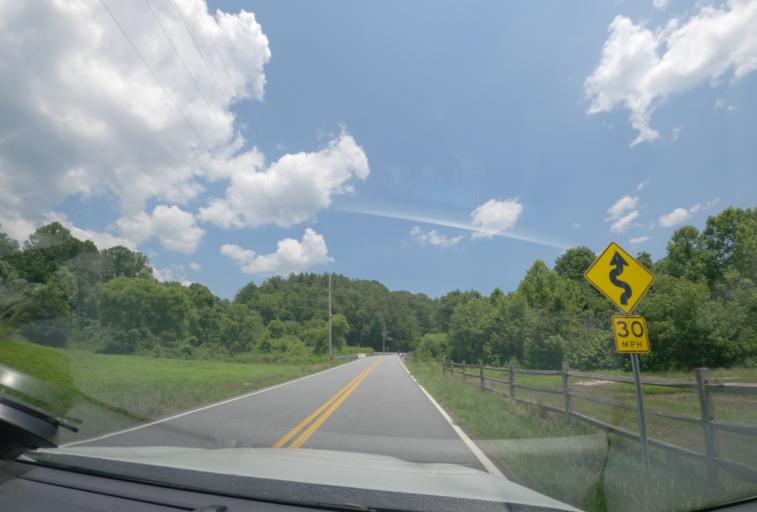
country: US
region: South Carolina
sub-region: Pickens County
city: Pickens
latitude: 34.9804
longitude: -82.8538
